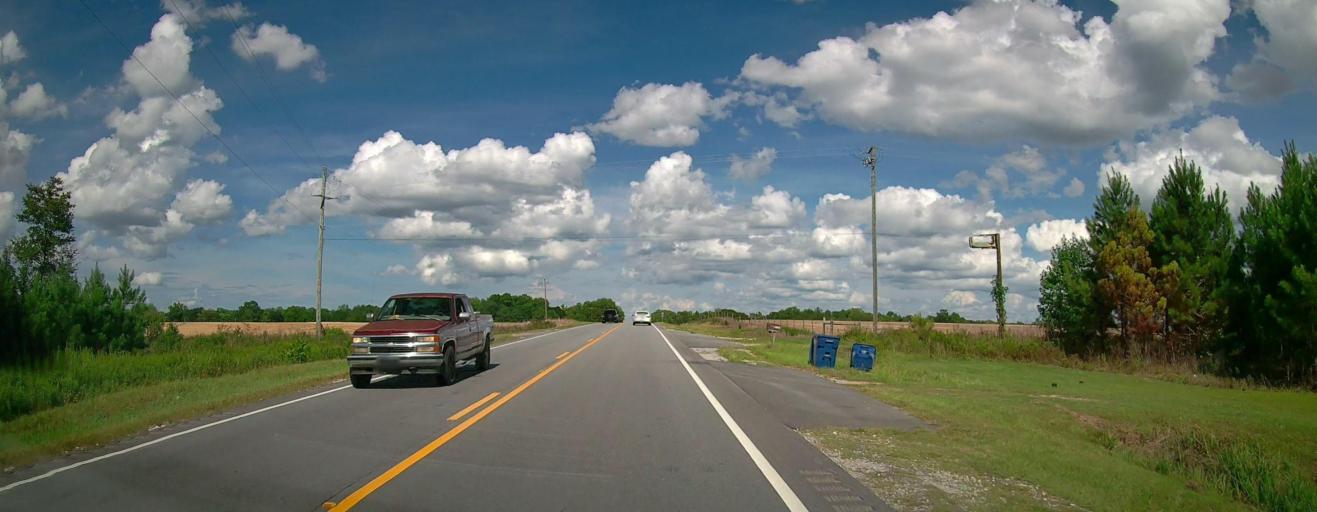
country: US
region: Alabama
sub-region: Lee County
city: Auburn
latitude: 32.4349
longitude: -85.4105
